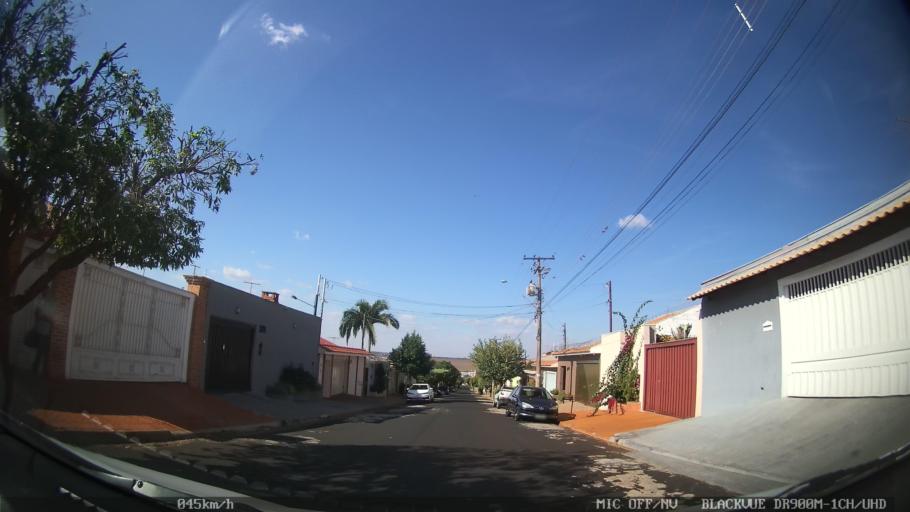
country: BR
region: Sao Paulo
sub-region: Ribeirao Preto
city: Ribeirao Preto
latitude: -21.1757
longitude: -47.7664
